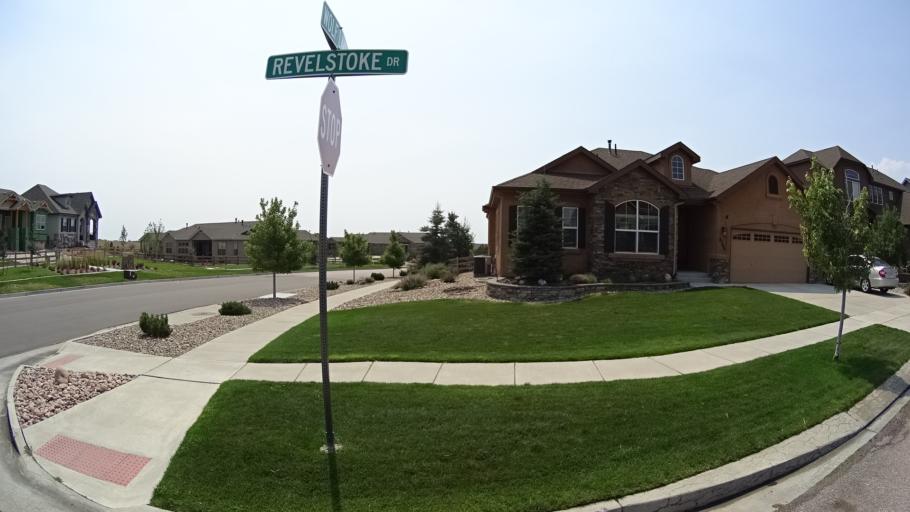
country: US
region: Colorado
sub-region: El Paso County
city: Black Forest
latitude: 38.9690
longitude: -104.7148
